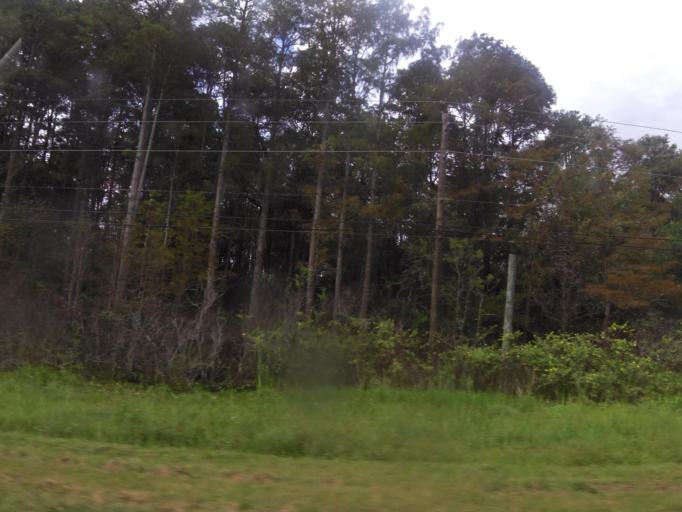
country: US
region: Florida
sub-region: Saint Johns County
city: Butler Beach
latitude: 29.7568
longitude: -81.3004
